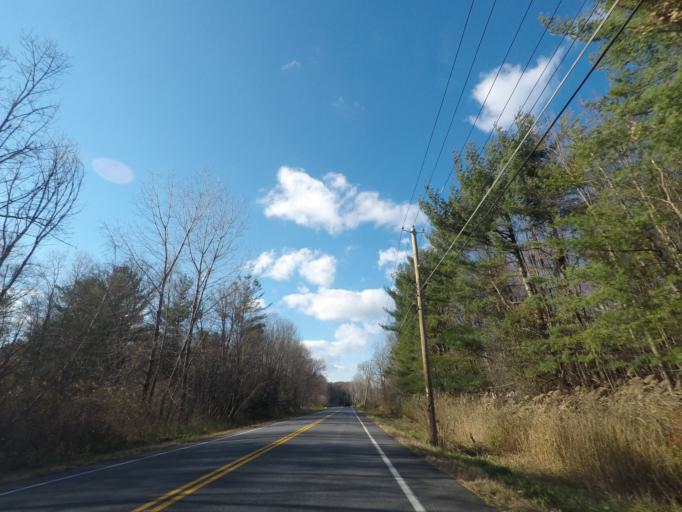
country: US
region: New York
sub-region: Saratoga County
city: Country Knolls
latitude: 42.8875
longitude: -73.8012
